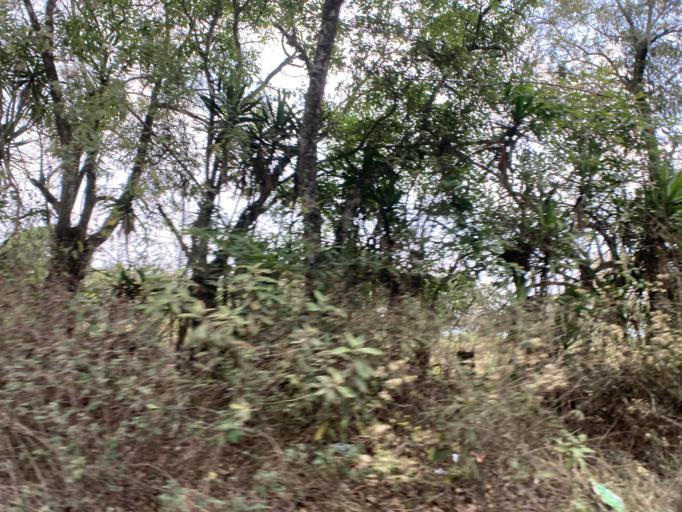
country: GT
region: Guatemala
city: Villa Canales
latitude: 14.4367
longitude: -90.5064
